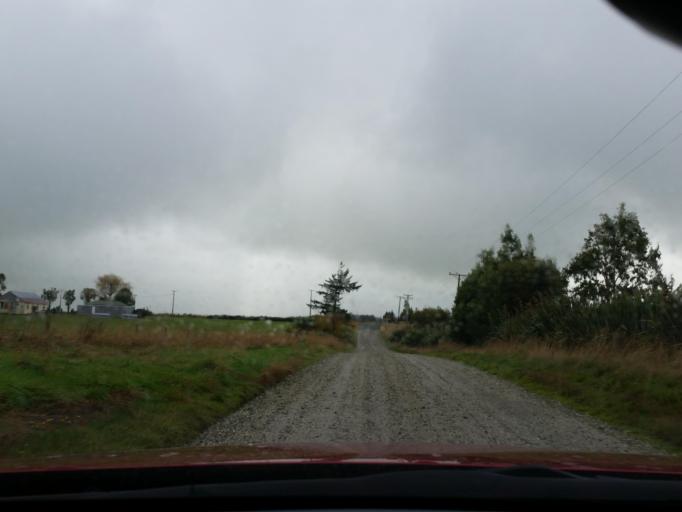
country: NZ
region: Southland
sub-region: Invercargill City
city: Invercargill
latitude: -46.2773
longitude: 168.5563
